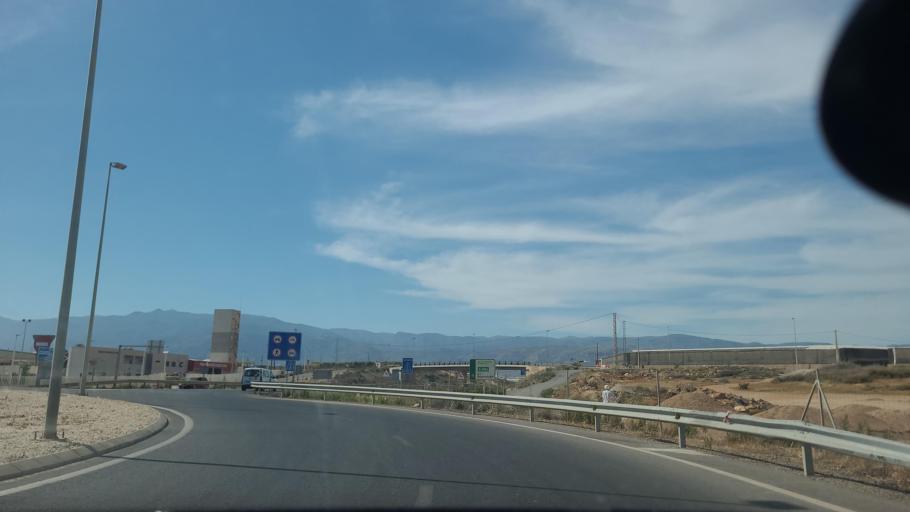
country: ES
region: Andalusia
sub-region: Provincia de Almeria
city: Roquetas de Mar
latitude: 36.7497
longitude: -2.6360
